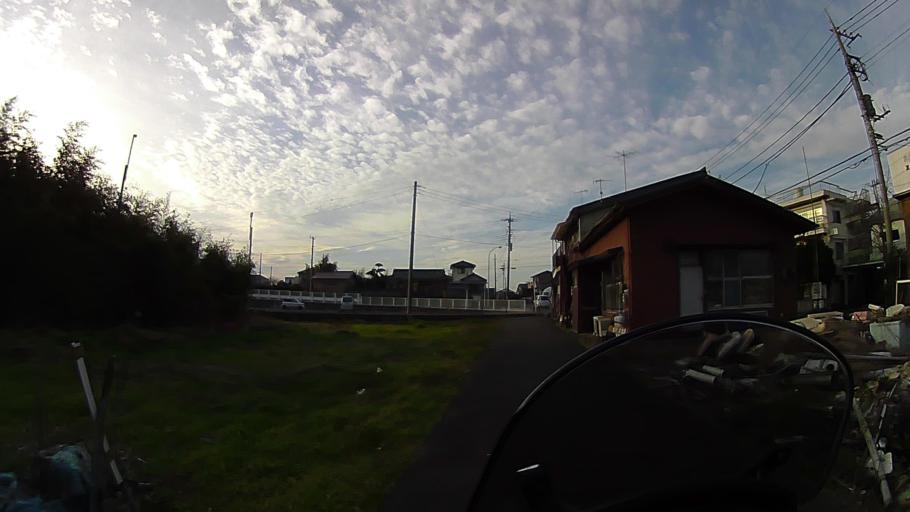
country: JP
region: Kanagawa
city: Atsugi
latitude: 35.4245
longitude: 139.4192
